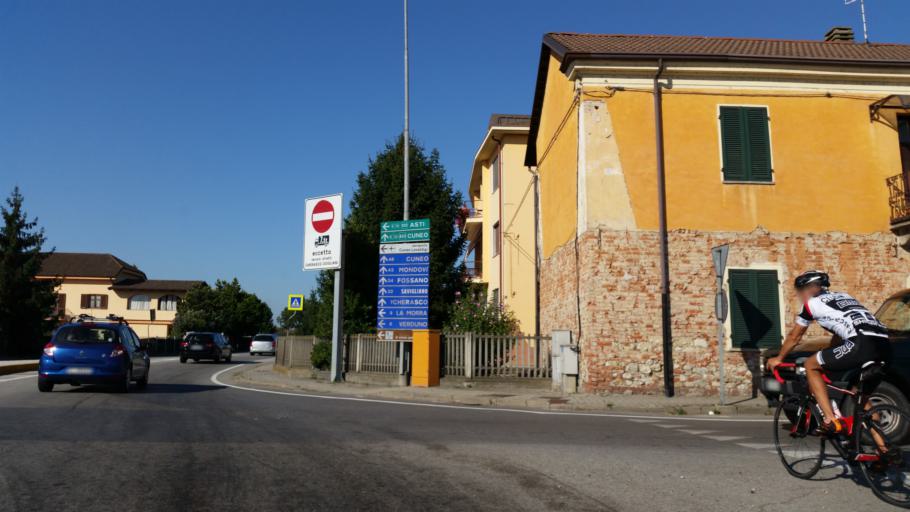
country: IT
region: Piedmont
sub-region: Provincia di Cuneo
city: Cinzano
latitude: 44.6870
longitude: 7.8960
